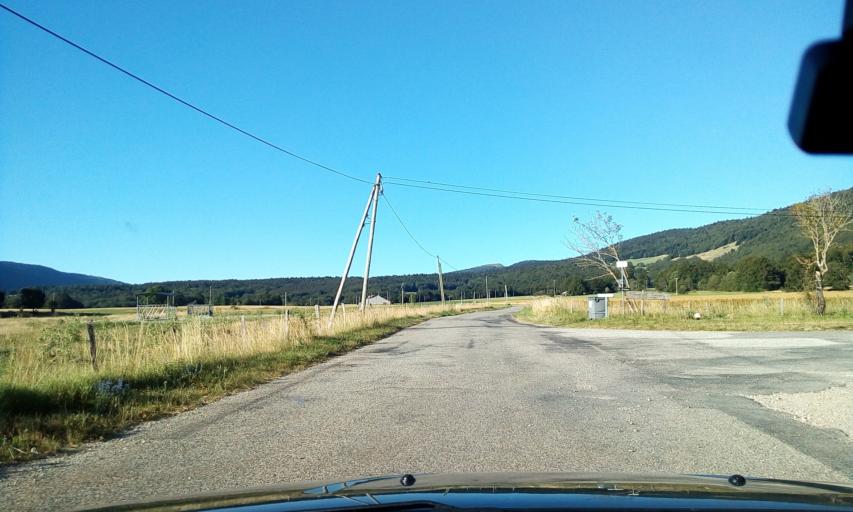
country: FR
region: Rhone-Alpes
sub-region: Departement de la Drome
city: Die
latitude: 44.8772
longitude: 5.3631
